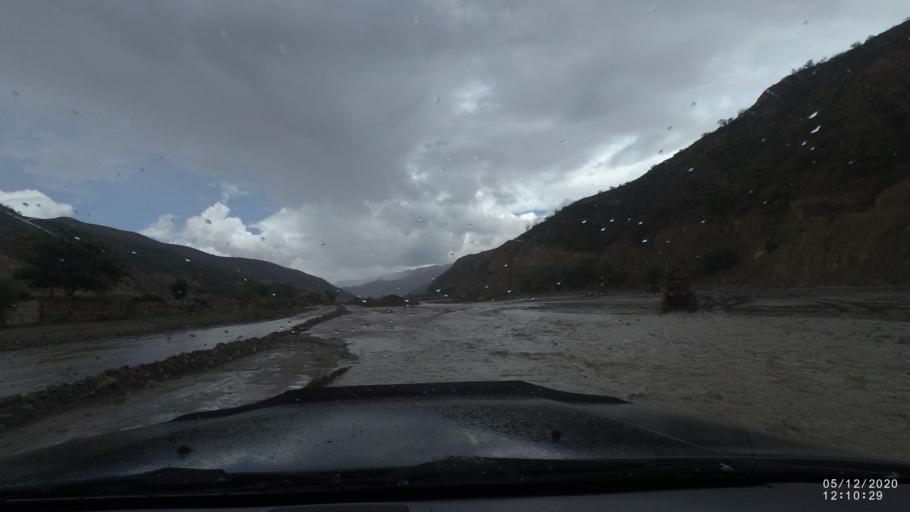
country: BO
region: Cochabamba
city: Sipe Sipe
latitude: -17.5673
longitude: -66.3715
